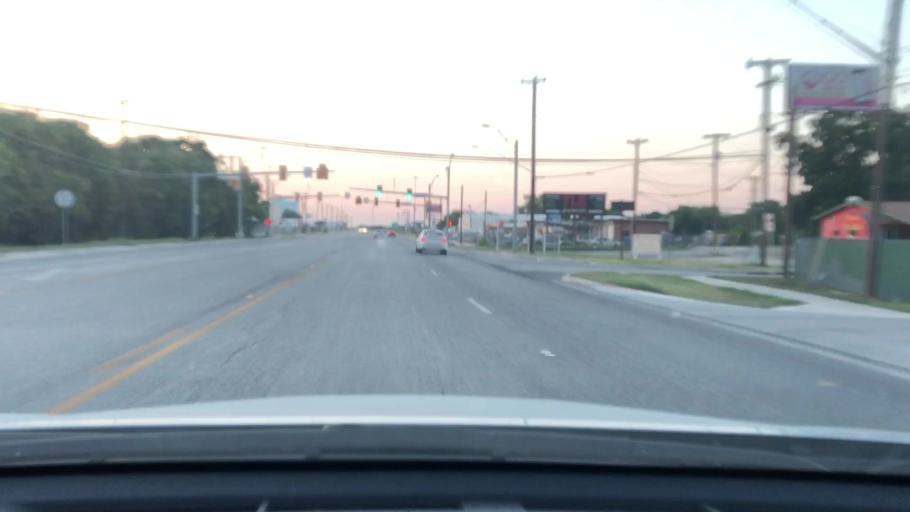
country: US
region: Texas
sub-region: Bexar County
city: Kirby
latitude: 29.4400
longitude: -98.4051
